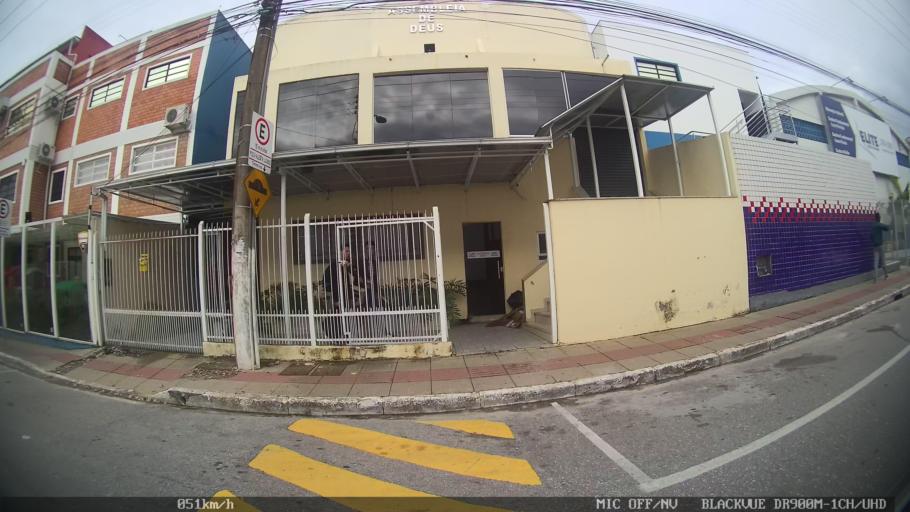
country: BR
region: Santa Catarina
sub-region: Sao Jose
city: Campinas
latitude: -27.5538
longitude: -48.6210
